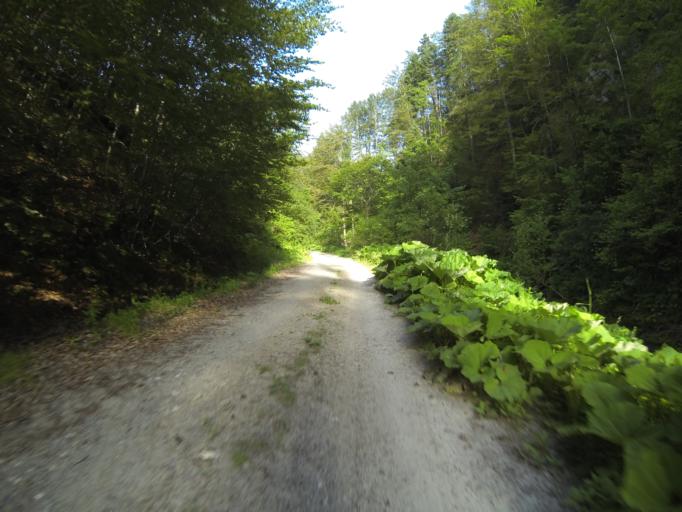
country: RO
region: Valcea
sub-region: Comuna Barbatesti
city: Barbatesti
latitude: 45.2585
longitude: 24.1640
